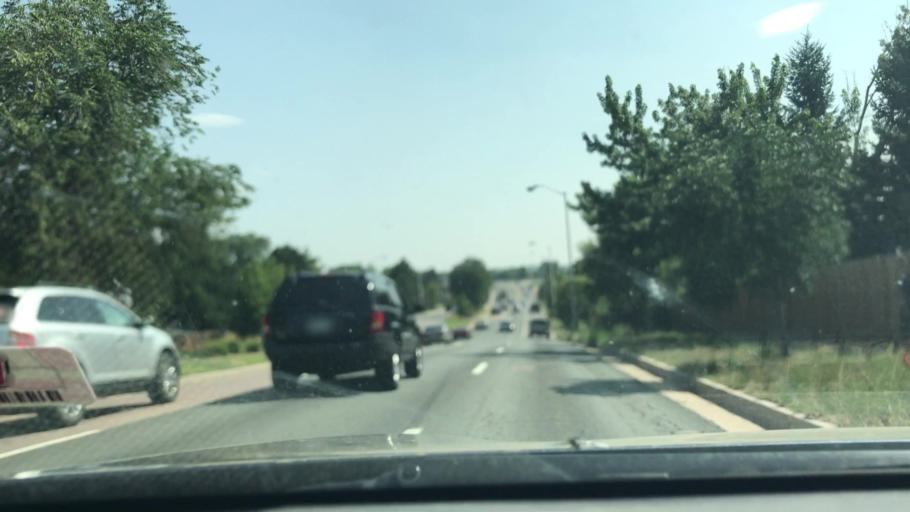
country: US
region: Colorado
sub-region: El Paso County
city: Colorado Springs
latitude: 38.9196
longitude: -104.7754
